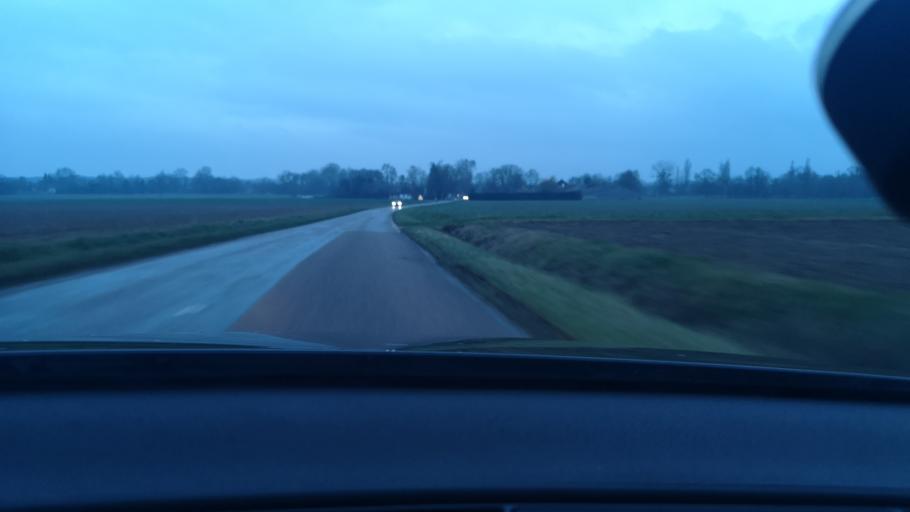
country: FR
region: Bourgogne
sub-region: Departement de la Cote-d'Or
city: Beaune
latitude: 47.0018
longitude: 4.9467
